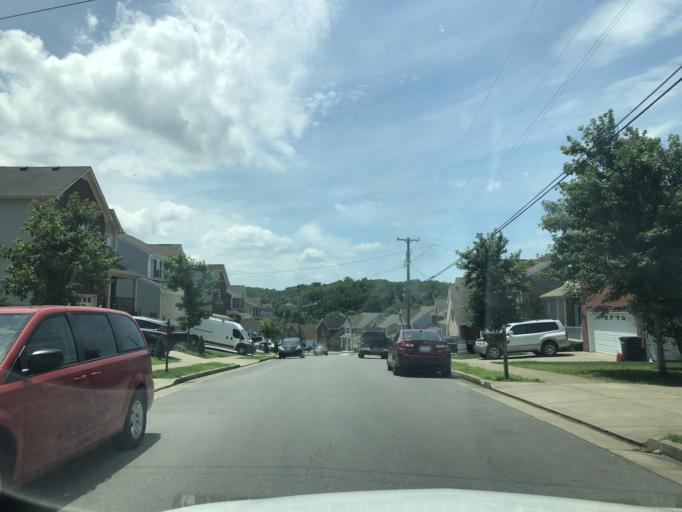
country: US
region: Tennessee
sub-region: Rutherford County
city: La Vergne
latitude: 36.0232
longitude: -86.6493
